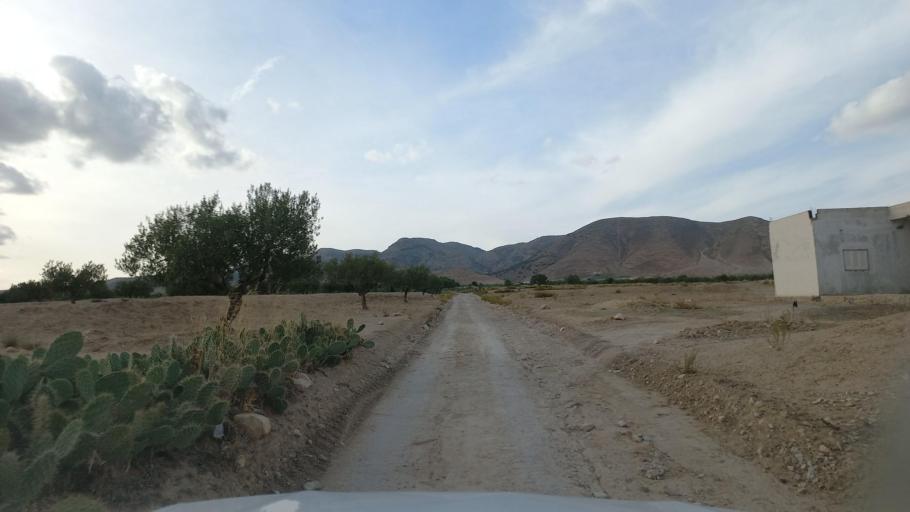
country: TN
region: Al Qasrayn
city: Sbiba
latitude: 35.4428
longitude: 9.0729
